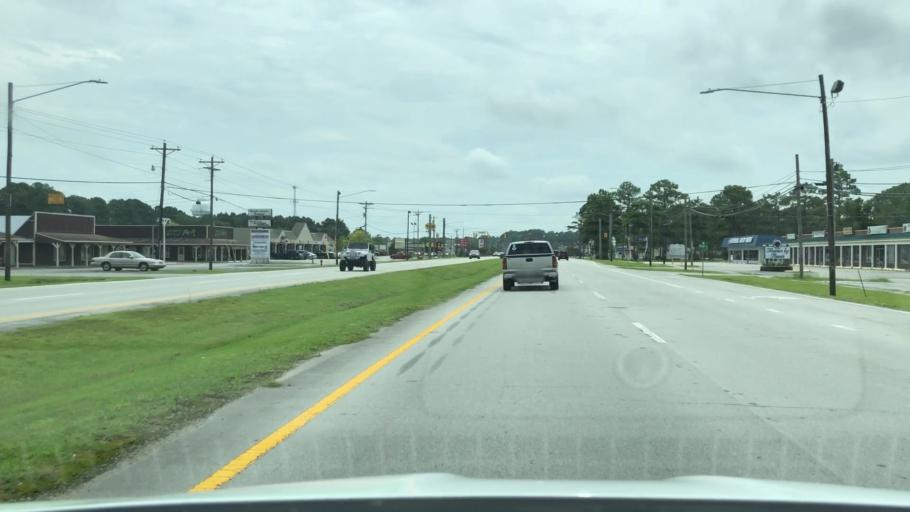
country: US
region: North Carolina
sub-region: Craven County
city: Havelock
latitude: 34.8653
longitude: -76.8990
